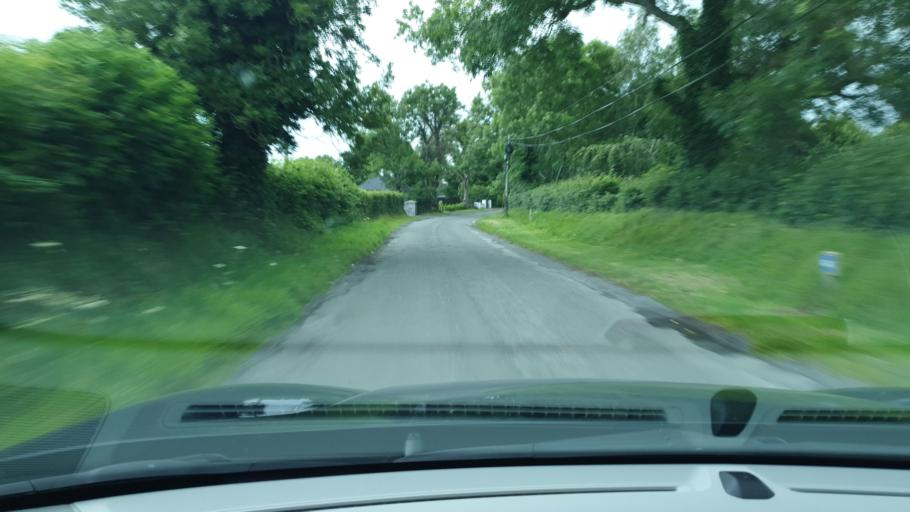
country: IE
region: Leinster
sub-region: An Mhi
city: Navan
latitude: 53.5913
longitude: -6.6305
